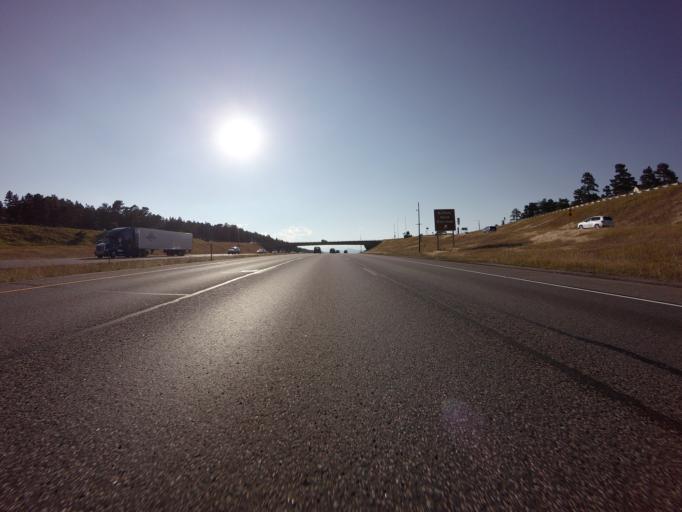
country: US
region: Colorado
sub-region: Jefferson County
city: Genesee
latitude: 39.7099
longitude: -105.2930
